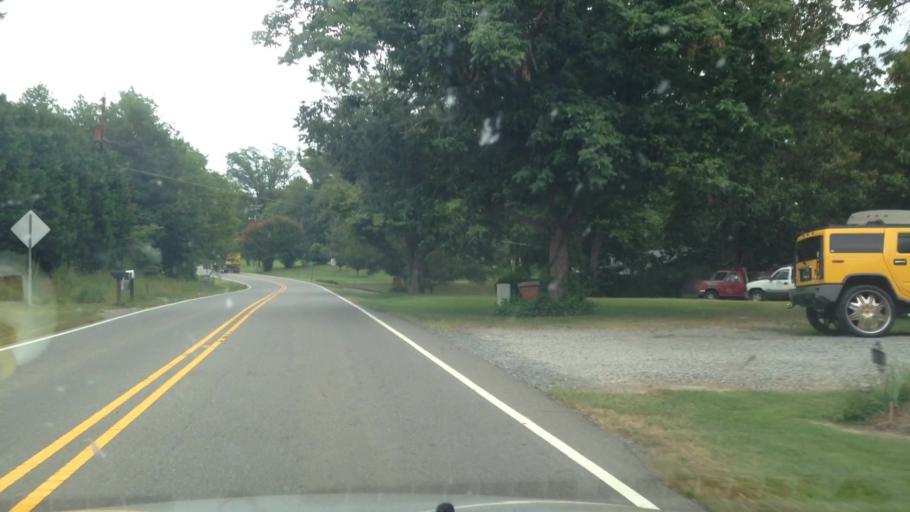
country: US
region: North Carolina
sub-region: Rockingham County
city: Wentworth
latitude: 36.4007
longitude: -79.7765
